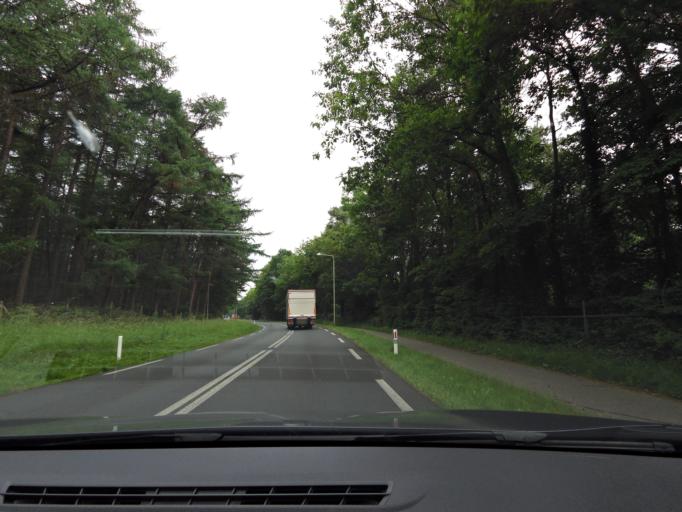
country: NL
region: Gelderland
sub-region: Gemeente Brummen
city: Eerbeek
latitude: 52.0919
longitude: 6.0628
